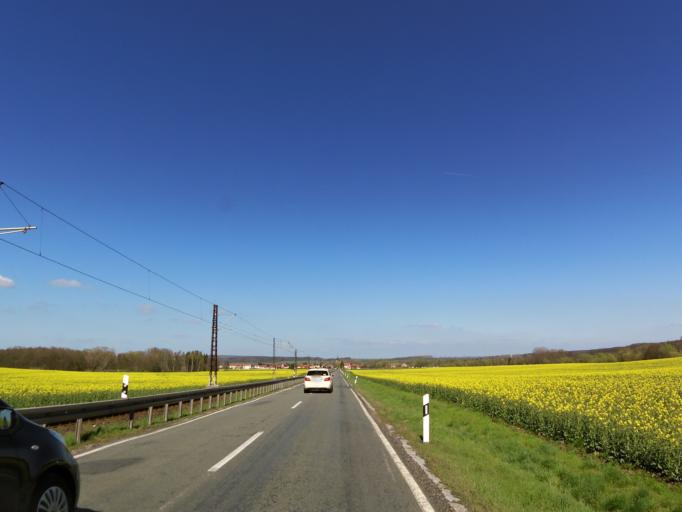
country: DE
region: Thuringia
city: Horselgau
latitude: 50.8917
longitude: 10.5874
